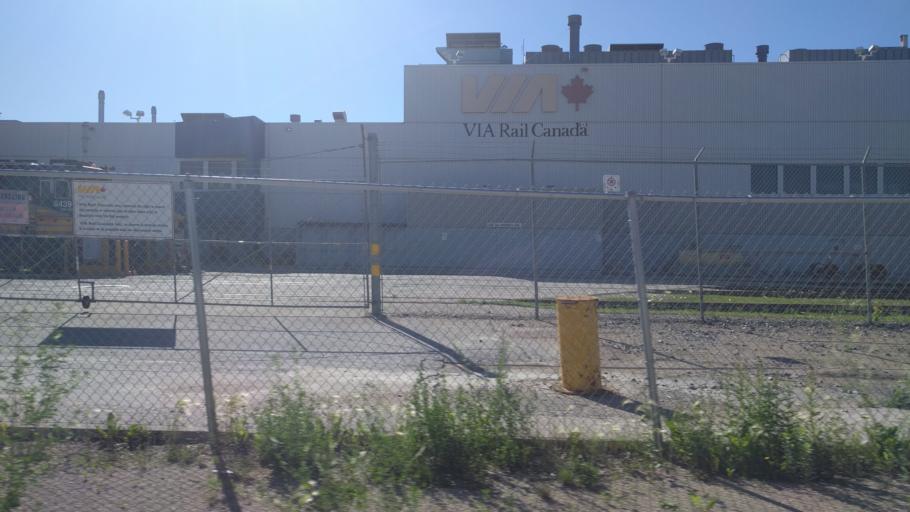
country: CA
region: Manitoba
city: Winnipeg
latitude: 49.8680
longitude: -97.1421
